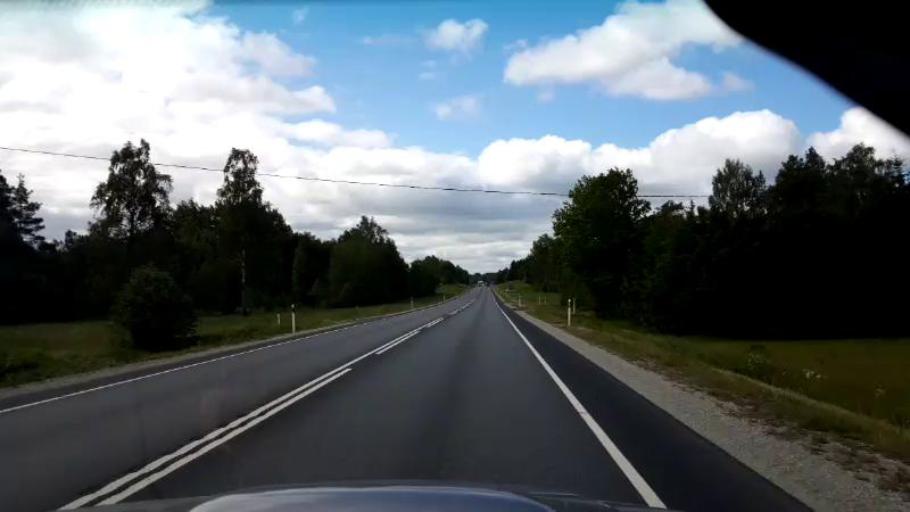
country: EE
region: Harju
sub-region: Nissi vald
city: Riisipere
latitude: 59.0544
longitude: 24.4462
